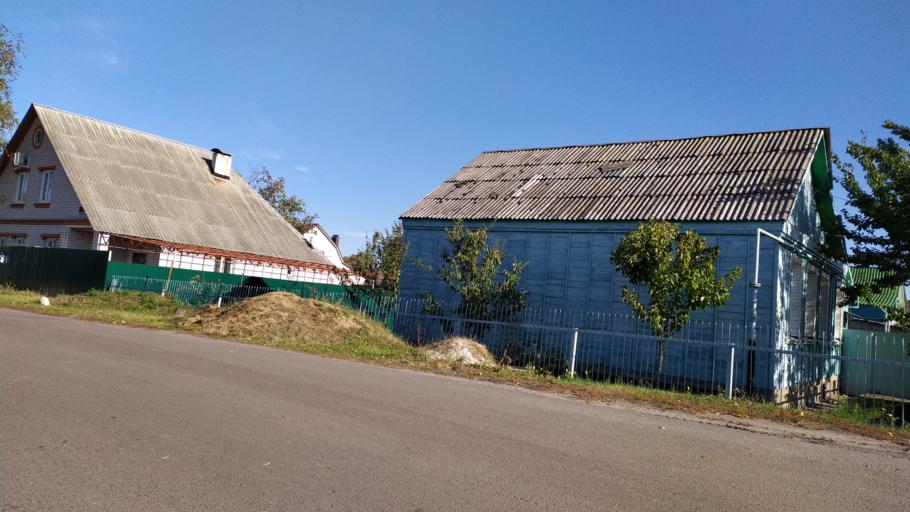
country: RU
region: Kursk
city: Kursk
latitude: 51.6421
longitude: 36.1404
